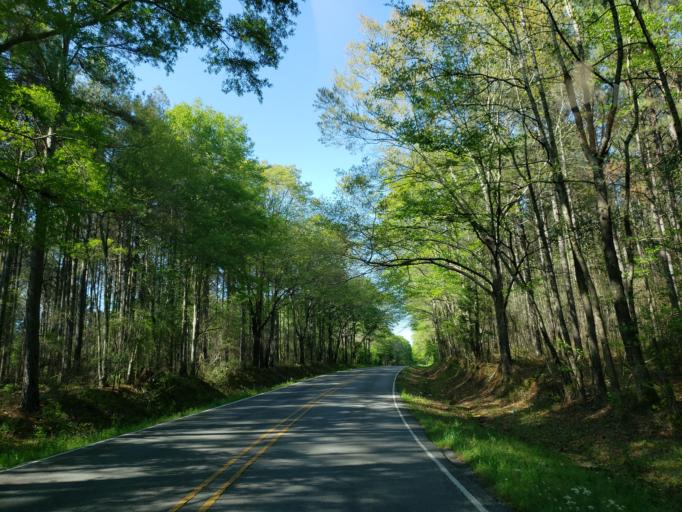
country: US
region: Mississippi
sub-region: Forrest County
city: Rawls Springs
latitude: 31.5078
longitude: -89.3603
